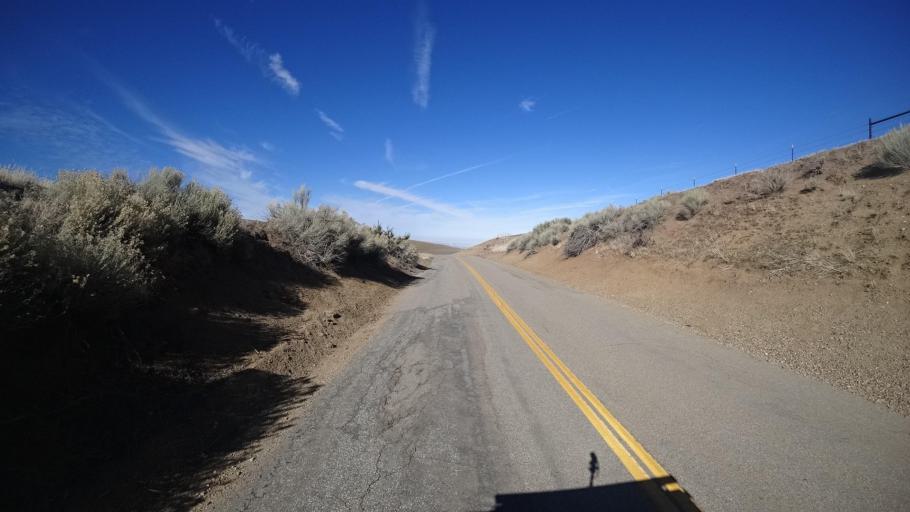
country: US
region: California
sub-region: Kern County
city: Maricopa
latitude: 34.9003
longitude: -119.3671
